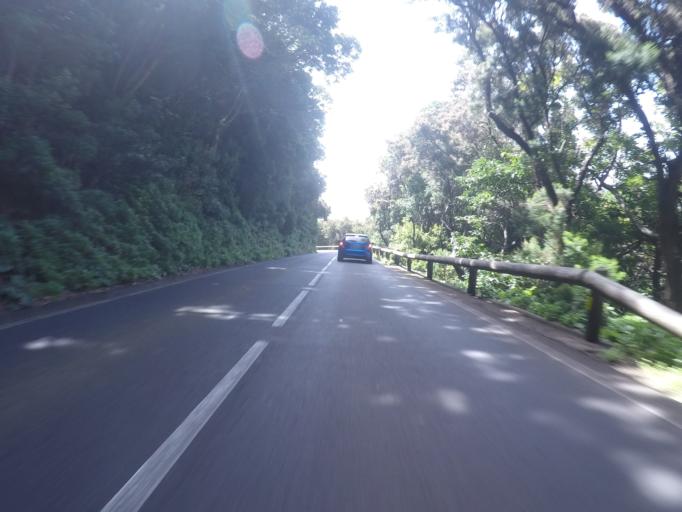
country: ES
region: Canary Islands
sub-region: Provincia de Santa Cruz de Tenerife
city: Santa Cruz de Tenerife
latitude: 28.5350
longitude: -16.2435
